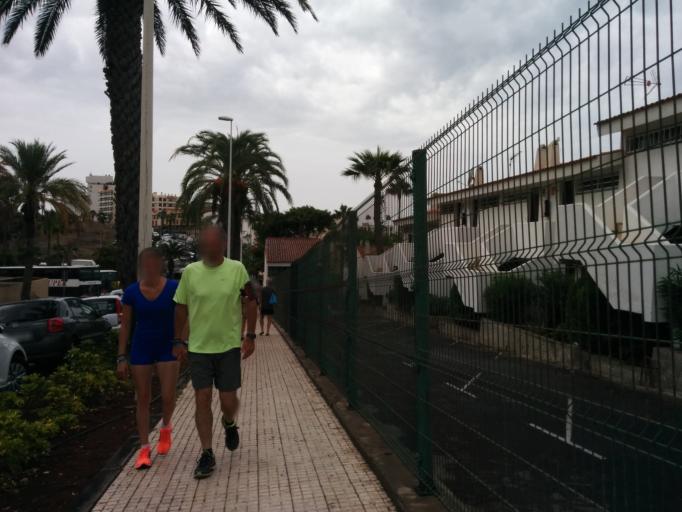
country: ES
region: Canary Islands
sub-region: Provincia de Santa Cruz de Tenerife
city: Playa de las Americas
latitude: 28.0674
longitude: -16.7278
